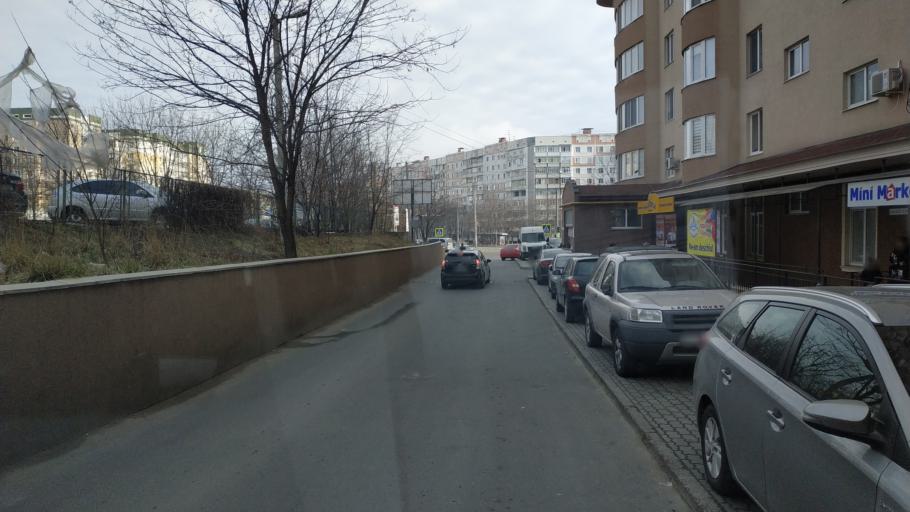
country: MD
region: Chisinau
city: Vatra
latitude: 47.0381
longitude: 28.7686
